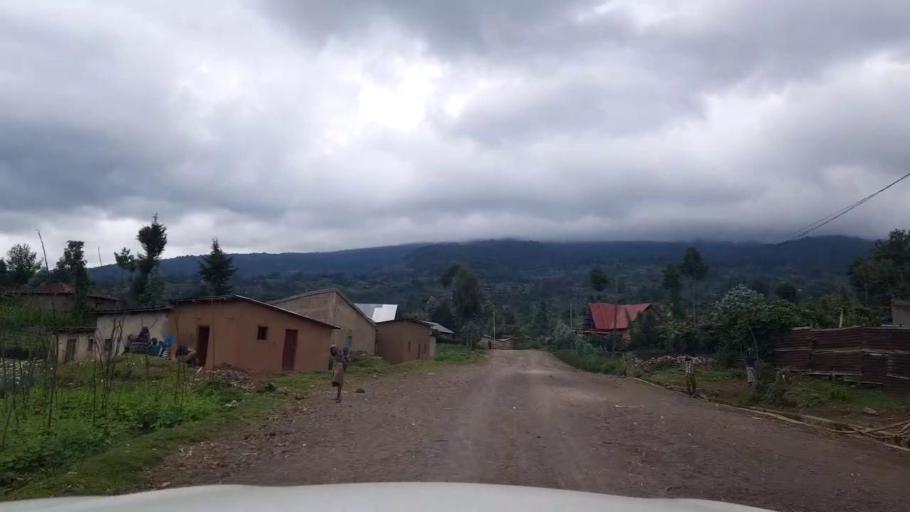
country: RW
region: Northern Province
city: Musanze
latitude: -1.5422
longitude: 29.5327
